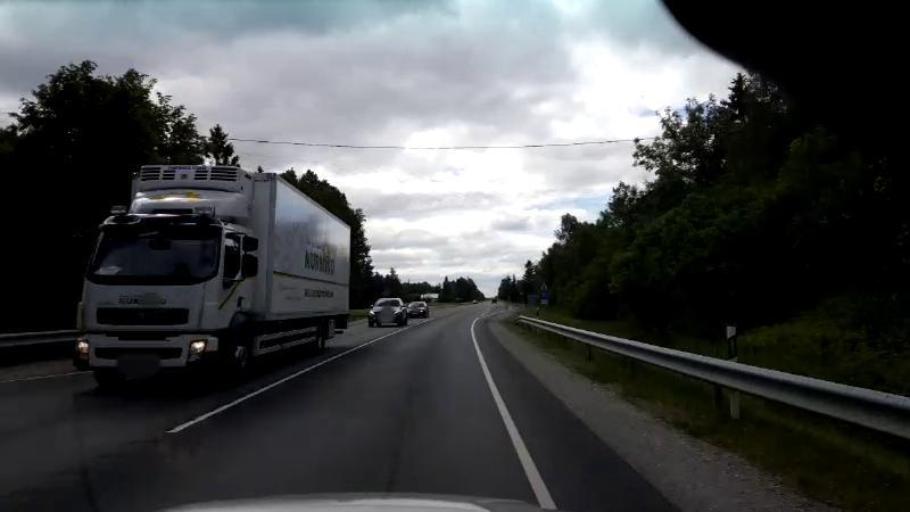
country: EE
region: Paernumaa
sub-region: Halinga vald
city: Parnu-Jaagupi
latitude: 58.6558
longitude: 24.4747
